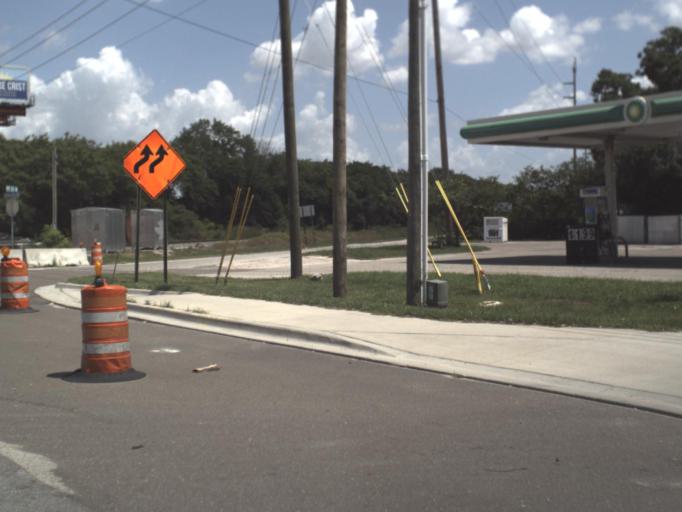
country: US
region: Florida
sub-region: Pinellas County
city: Largo
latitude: 27.8945
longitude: -82.7722
